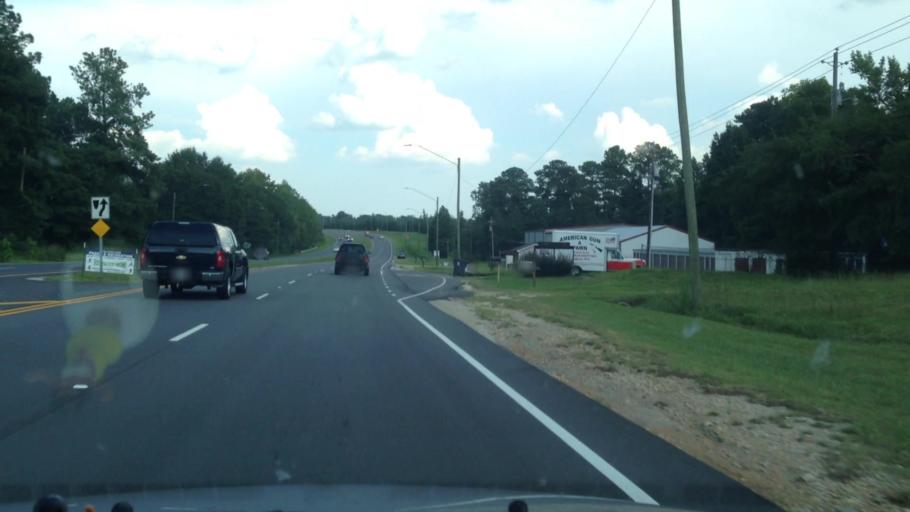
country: US
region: North Carolina
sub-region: Harnett County
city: Lillington
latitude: 35.4149
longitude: -78.7974
